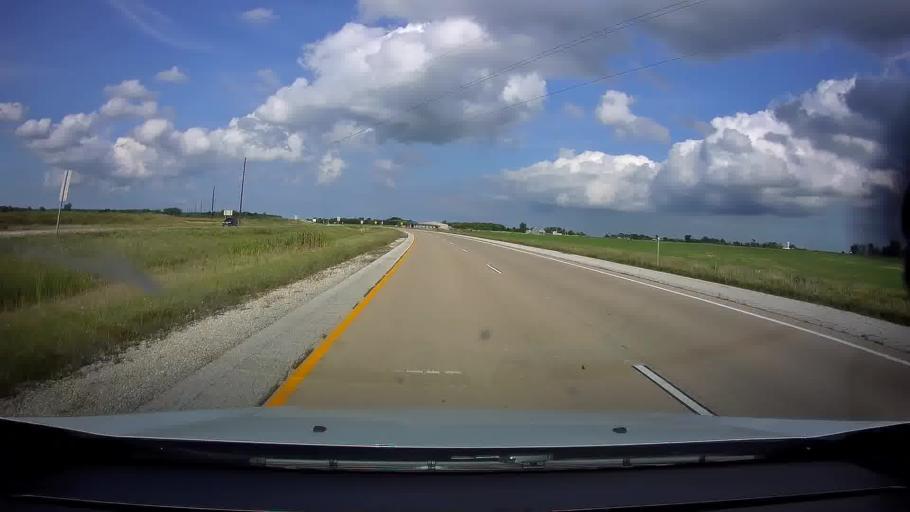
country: US
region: Wisconsin
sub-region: Kewaunee County
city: Luxemburg
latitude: 44.7177
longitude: -87.6188
